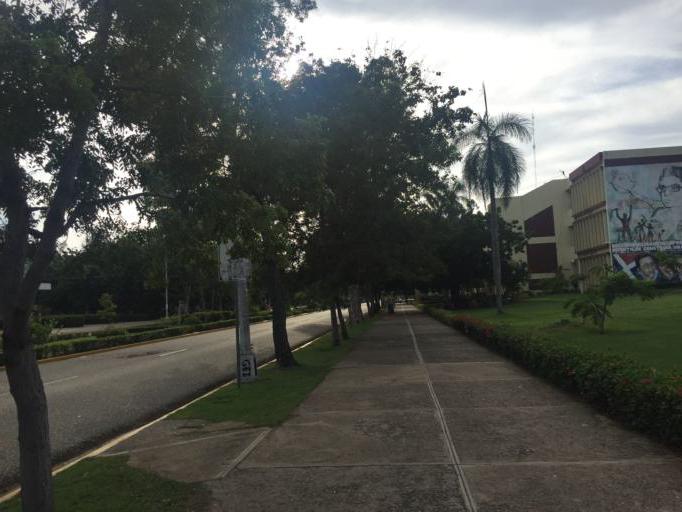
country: DO
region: Nacional
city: Ciudad Nueva
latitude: 18.4618
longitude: -69.9159
